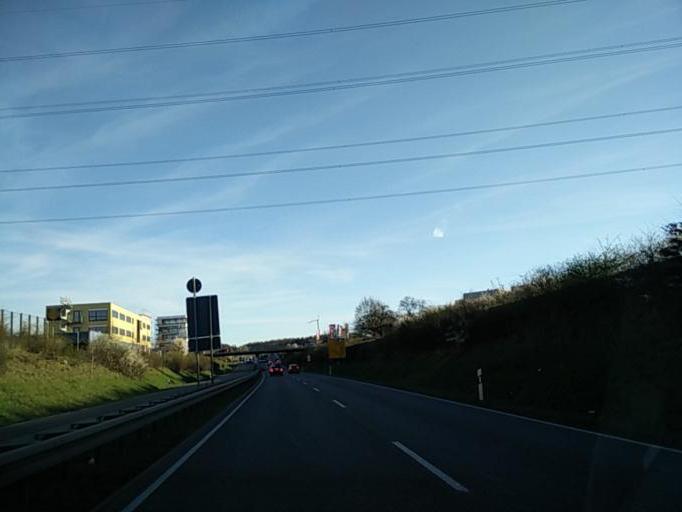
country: DE
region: Baden-Wuerttemberg
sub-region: Regierungsbezirk Stuttgart
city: Holzgerlingen
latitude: 48.6448
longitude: 9.0083
